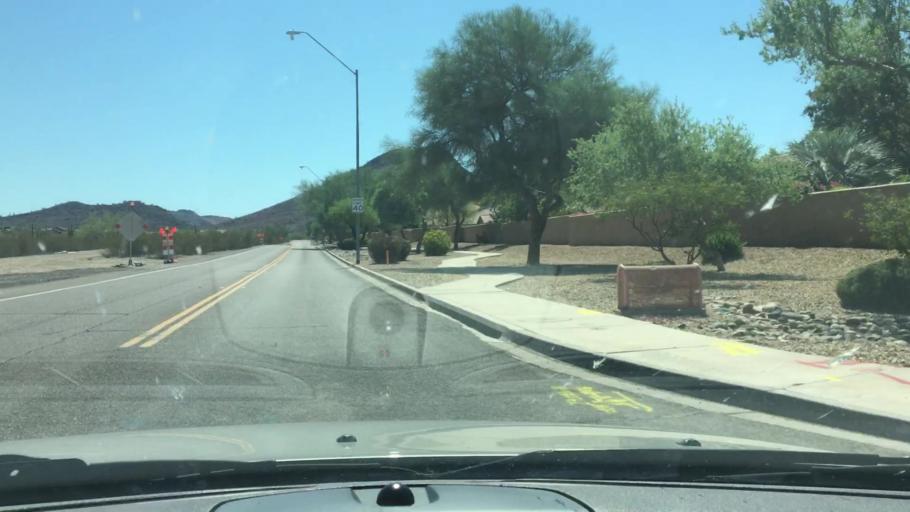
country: US
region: Arizona
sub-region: Maricopa County
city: Sun City
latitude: 33.7250
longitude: -112.2106
